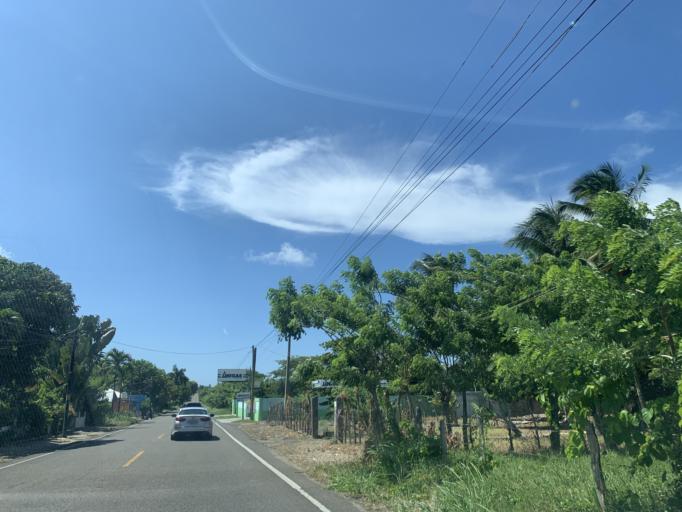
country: DO
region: Maria Trinidad Sanchez
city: Cabrera
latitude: 19.6668
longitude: -69.9477
